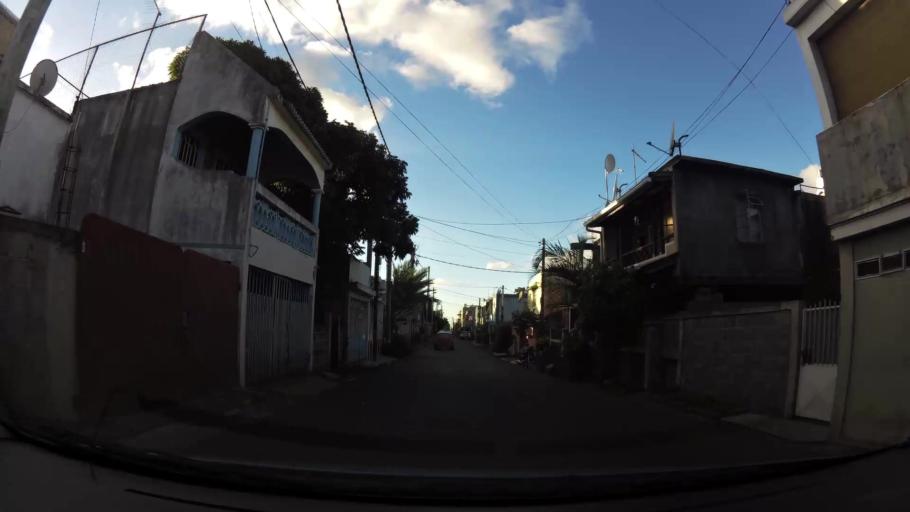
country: MU
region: Plaines Wilhems
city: Quatre Bornes
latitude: -20.2537
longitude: 57.4617
